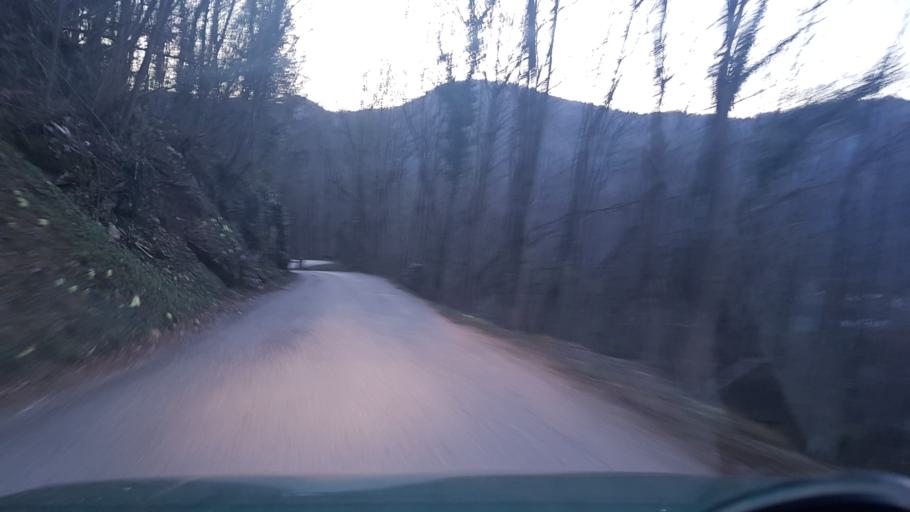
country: SI
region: Kanal
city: Kanal
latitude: 46.0746
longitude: 13.6408
